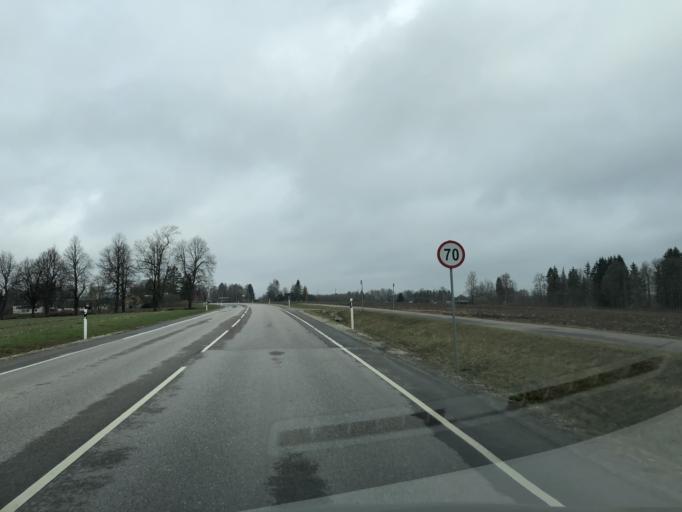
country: EE
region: Jogevamaa
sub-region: Tabivere vald
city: Tabivere
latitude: 58.6568
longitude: 26.5234
